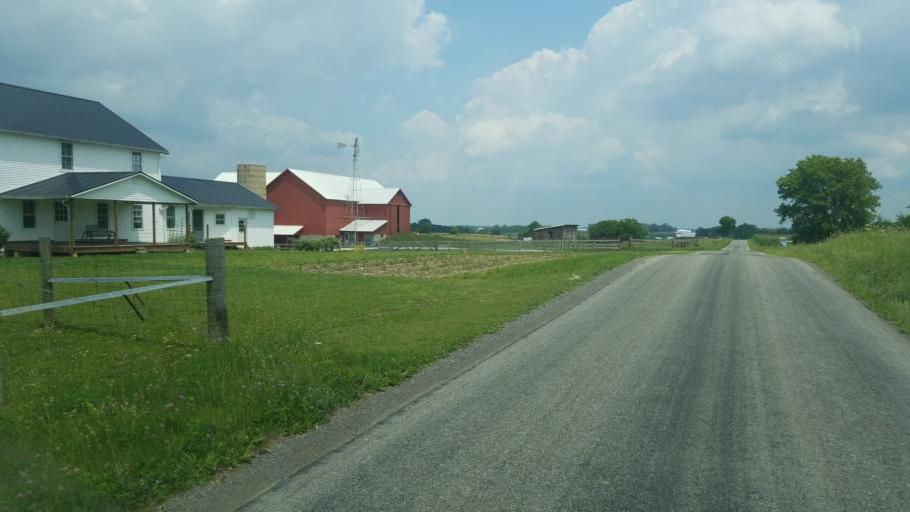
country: US
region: Ohio
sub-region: Hardin County
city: Kenton
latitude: 40.5927
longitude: -83.6306
